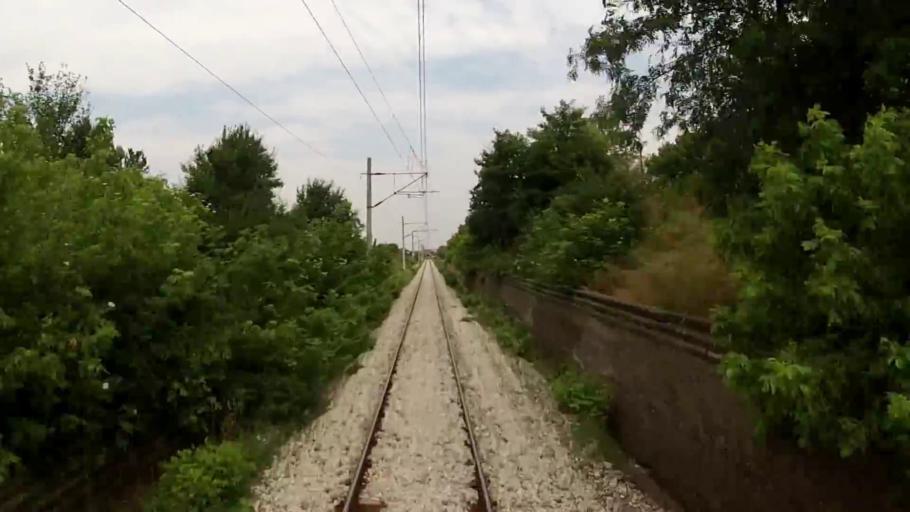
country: BG
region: Blagoevgrad
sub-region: Obshtina Blagoevgrad
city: Blagoevgrad
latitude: 41.9793
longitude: 23.0893
